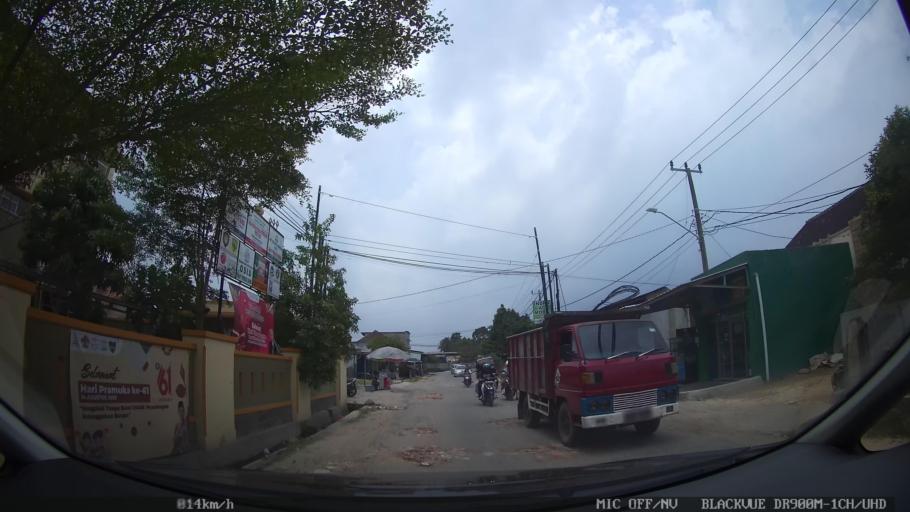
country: ID
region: Lampung
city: Kedaton
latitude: -5.3943
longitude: 105.3148
